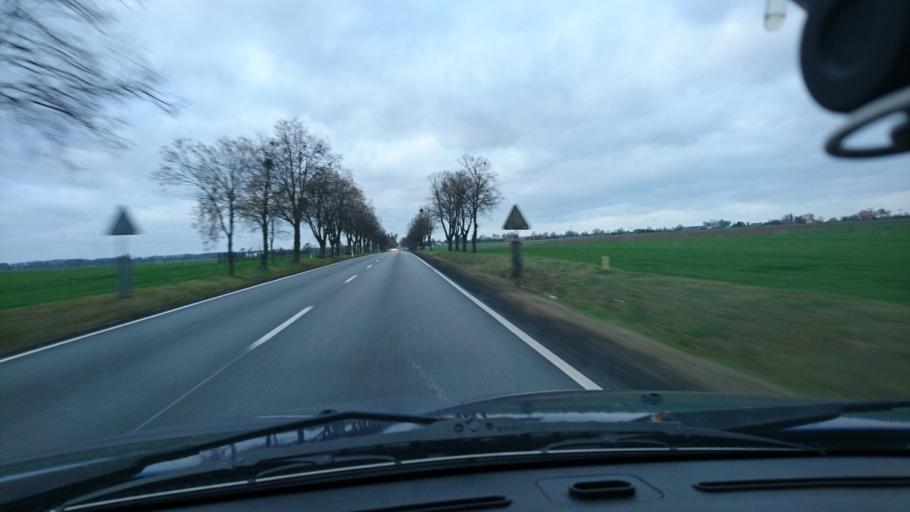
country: PL
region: Opole Voivodeship
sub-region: Powiat kluczborski
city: Kluczbork
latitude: 51.0182
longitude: 18.1980
